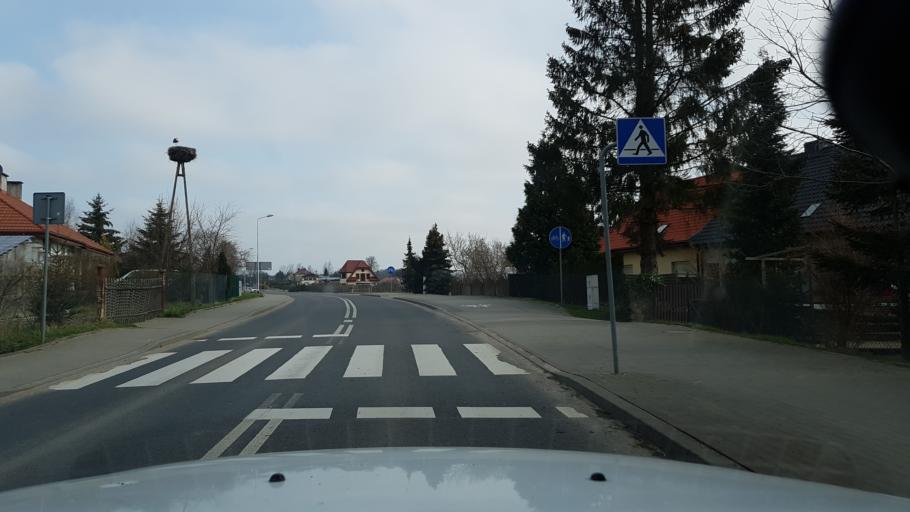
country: PL
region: West Pomeranian Voivodeship
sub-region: Powiat koszalinski
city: Sianow
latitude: 54.2611
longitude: 16.2664
